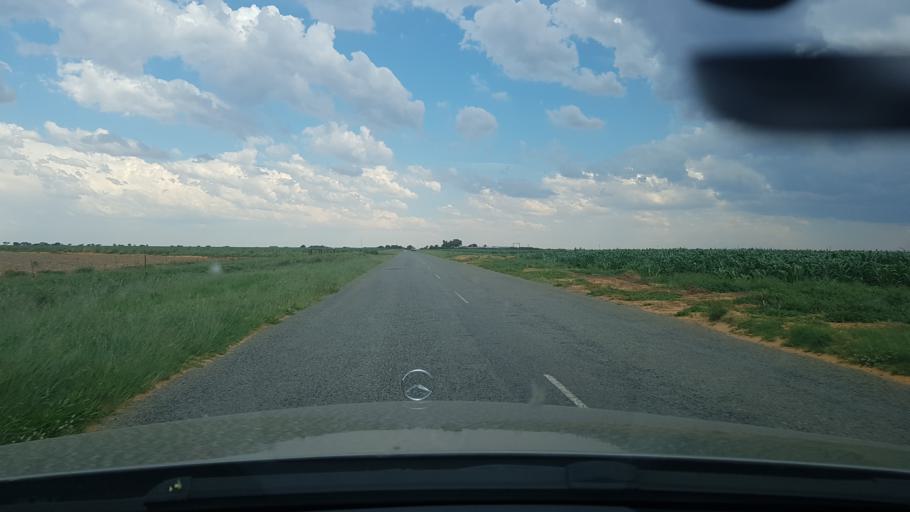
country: ZA
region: Orange Free State
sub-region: Lejweleputswa District Municipality
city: Hoopstad
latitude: -27.9109
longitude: 25.6805
